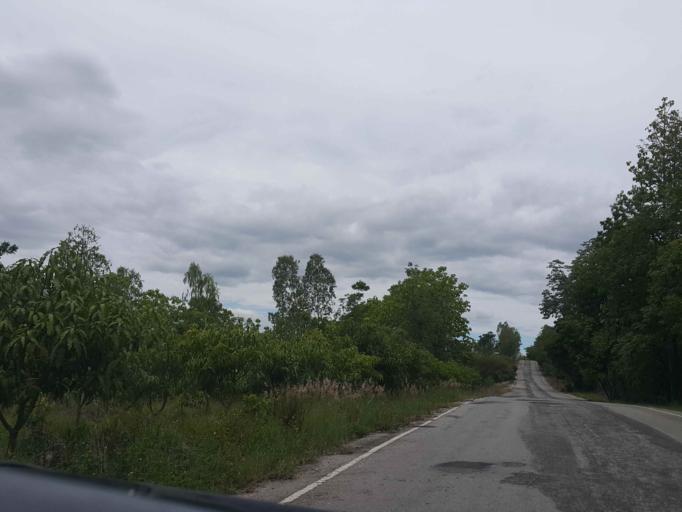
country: TH
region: Chiang Mai
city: Doi Lo
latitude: 18.5045
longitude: 98.7626
